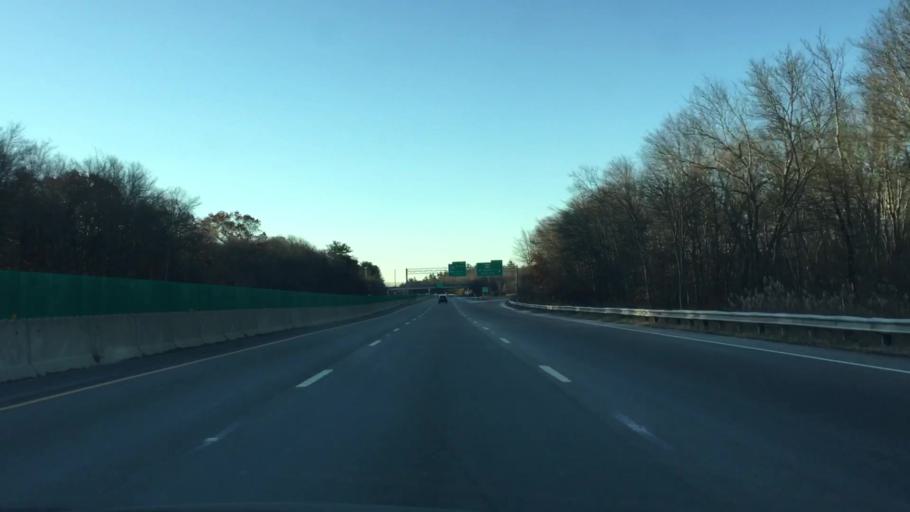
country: US
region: Massachusetts
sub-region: Bristol County
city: Raynham
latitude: 41.9711
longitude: -71.0270
